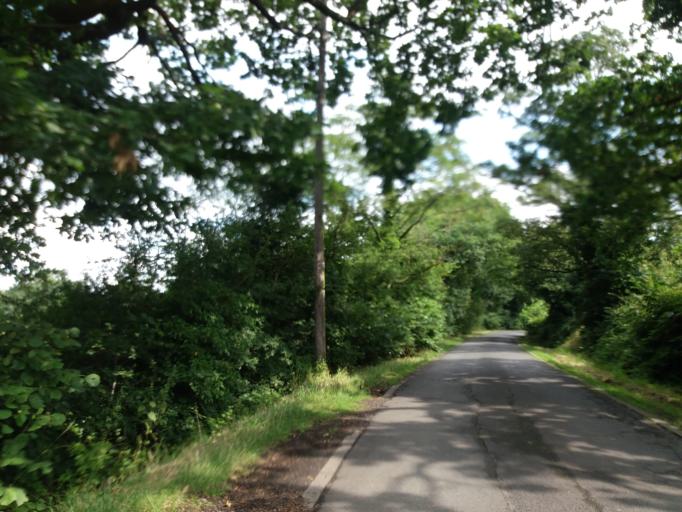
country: GB
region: England
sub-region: Lancashire
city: Euxton
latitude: 53.6658
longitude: -2.6665
